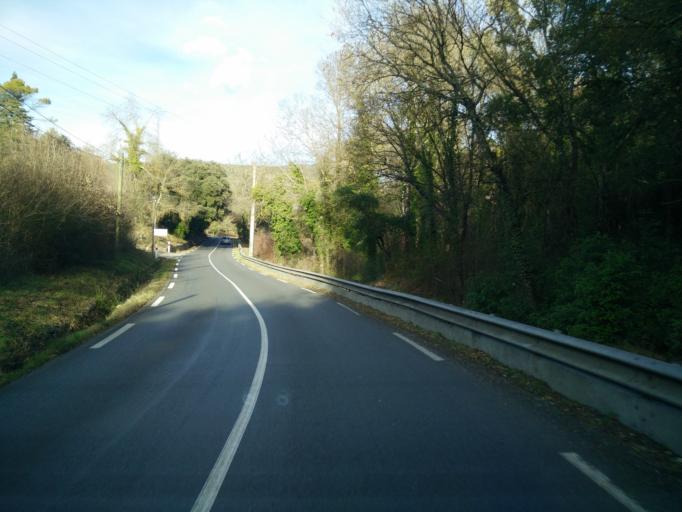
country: FR
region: Provence-Alpes-Cote d'Azur
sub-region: Departement des Alpes-Maritimes
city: Le Tignet
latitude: 43.6141
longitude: 6.8208
